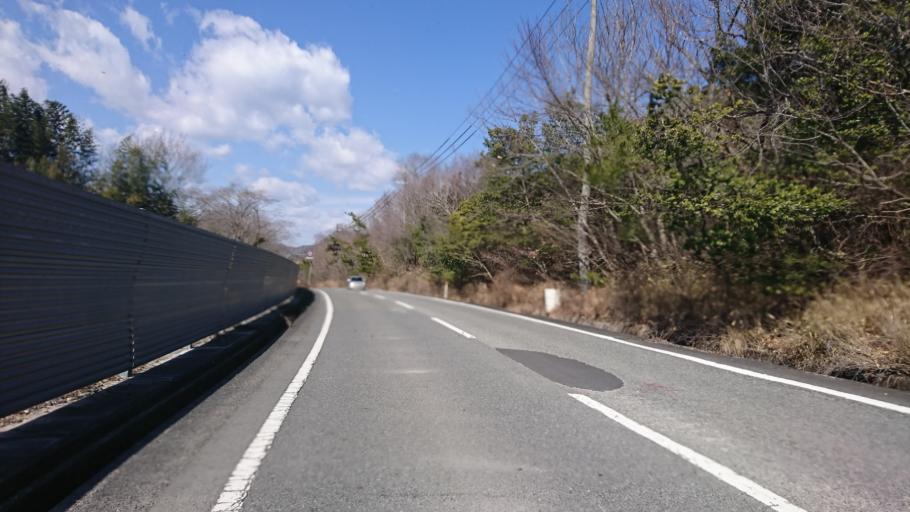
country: JP
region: Hyogo
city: Kakogawacho-honmachi
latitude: 34.8601
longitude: 134.8018
